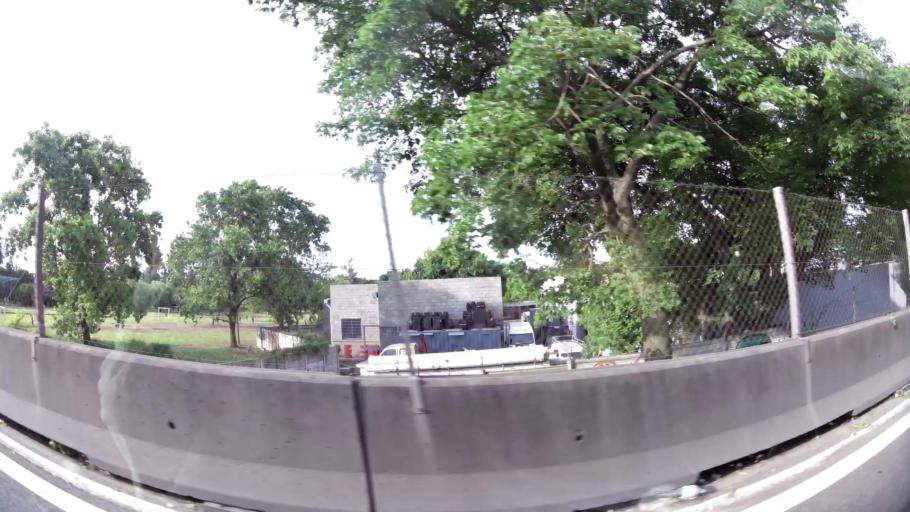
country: AR
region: Buenos Aires F.D.
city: Villa Lugano
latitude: -34.6474
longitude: -58.4803
